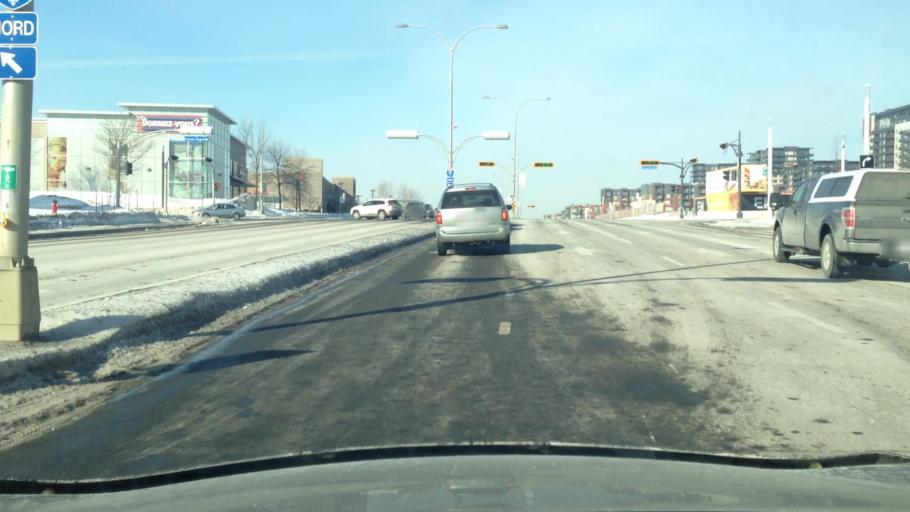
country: CA
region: Quebec
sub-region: Laval
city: Laval
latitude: 45.5554
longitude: -73.7229
